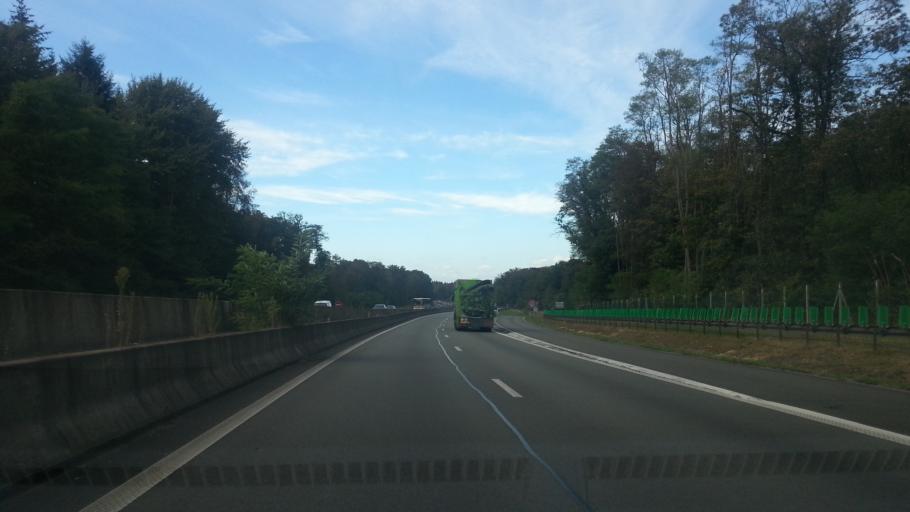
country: FR
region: Picardie
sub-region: Departement de l'Oise
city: Avilly-Saint-Leonard
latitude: 49.2285
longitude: 2.5406
